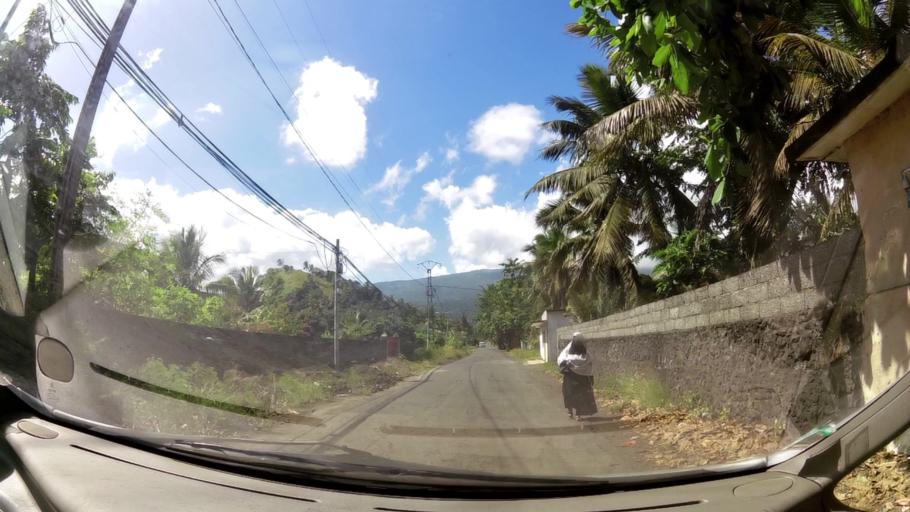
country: KM
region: Grande Comore
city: Mavingouni
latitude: -11.7413
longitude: 43.2400
